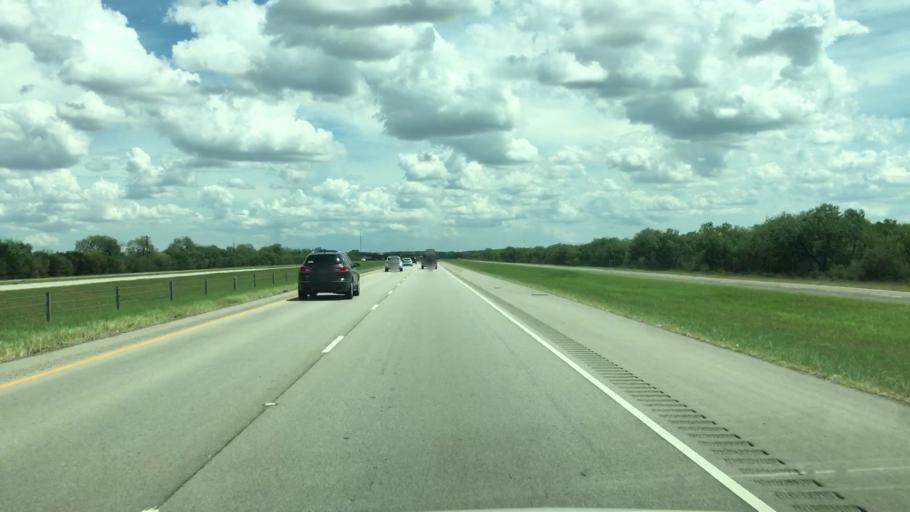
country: US
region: Texas
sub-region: Live Oak County
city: George West
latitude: 28.2786
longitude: -97.9535
